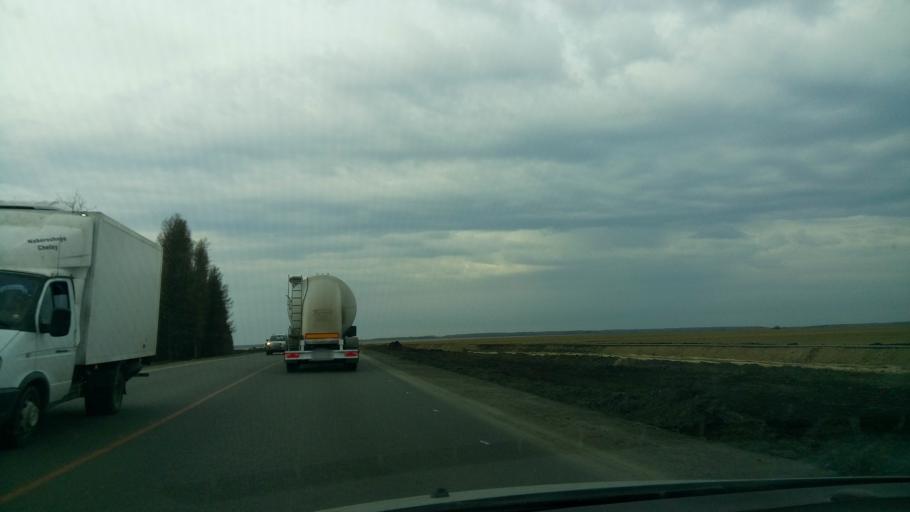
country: RU
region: Sverdlovsk
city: Kamyshlov
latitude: 56.8664
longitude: 62.9209
